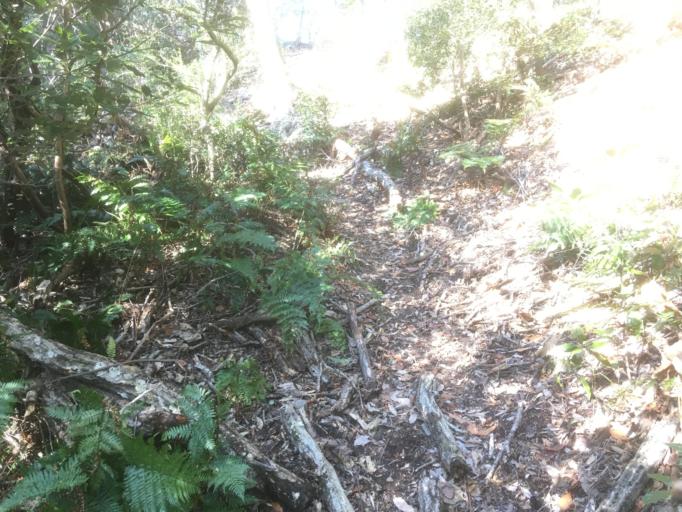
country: JP
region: Nara
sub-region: Ikoma-shi
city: Ikoma
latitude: 34.6930
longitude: 135.6823
